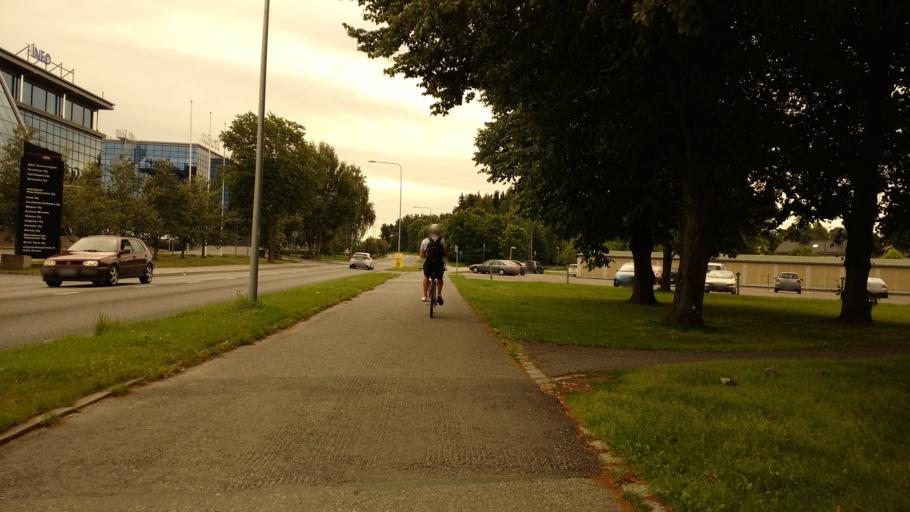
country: FI
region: Varsinais-Suomi
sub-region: Turku
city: Turku
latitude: 60.4429
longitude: 22.3075
